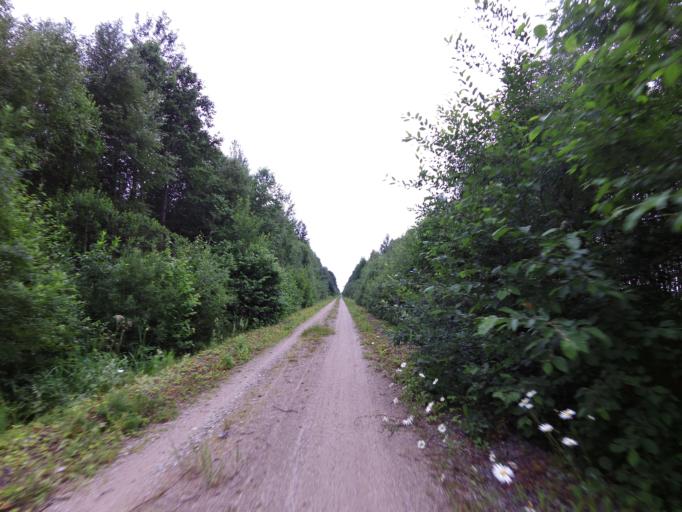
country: EE
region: Harju
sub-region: Nissi vald
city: Turba
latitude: 59.0199
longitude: 24.0978
